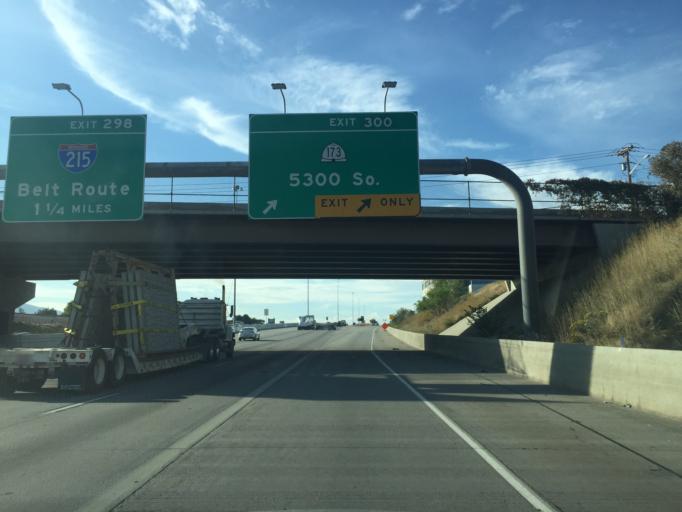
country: US
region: Utah
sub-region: Salt Lake County
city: Murray
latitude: 40.6612
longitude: -111.9016
